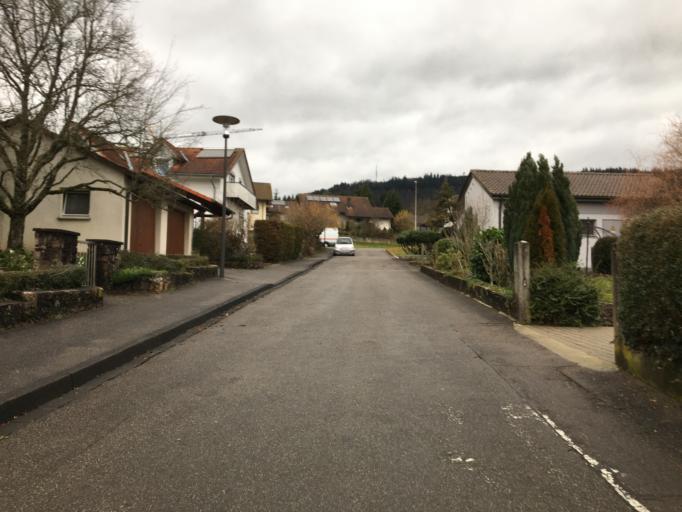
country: DE
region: Baden-Wuerttemberg
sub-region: Freiburg Region
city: Bad Sackingen
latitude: 47.5599
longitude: 7.9522
